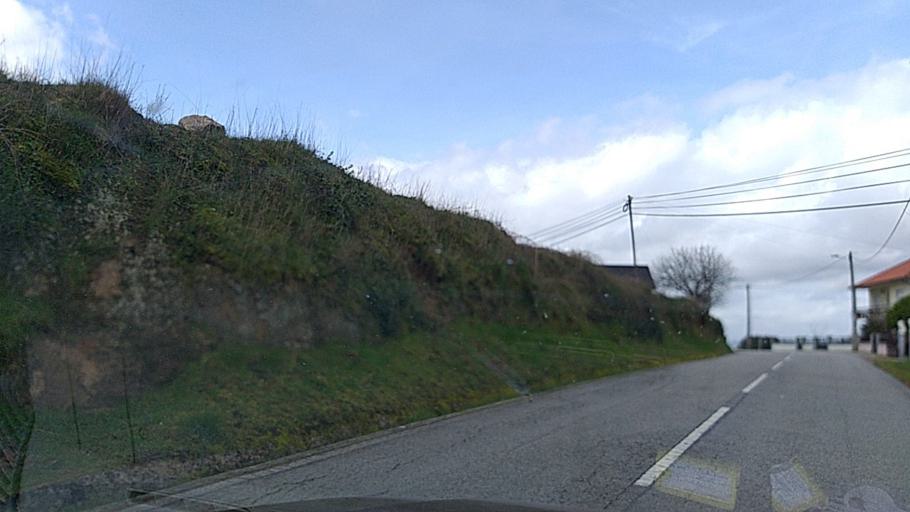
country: PT
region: Guarda
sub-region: Fornos de Algodres
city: Fornos de Algodres
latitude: 40.6658
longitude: -7.6186
